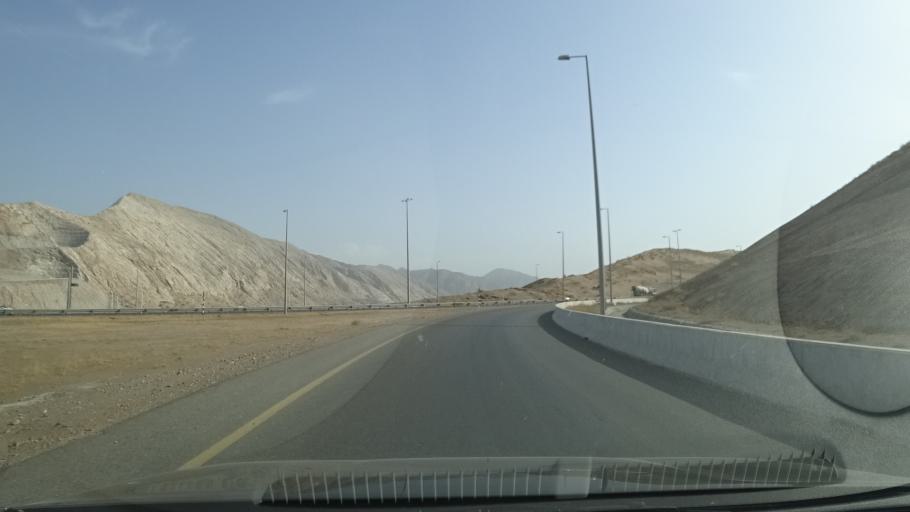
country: OM
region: Muhafazat Masqat
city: Bawshar
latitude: 23.5723
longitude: 58.4230
